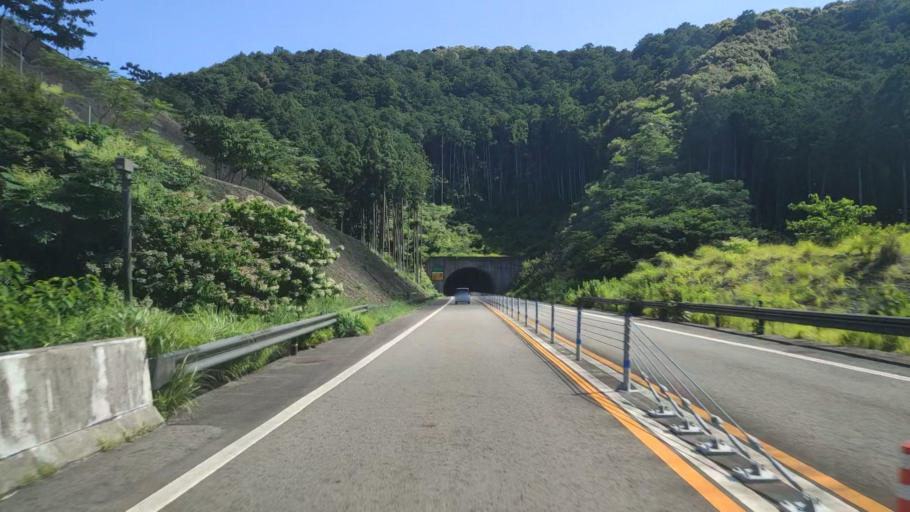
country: JP
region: Wakayama
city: Shingu
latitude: 33.6183
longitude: 135.9176
